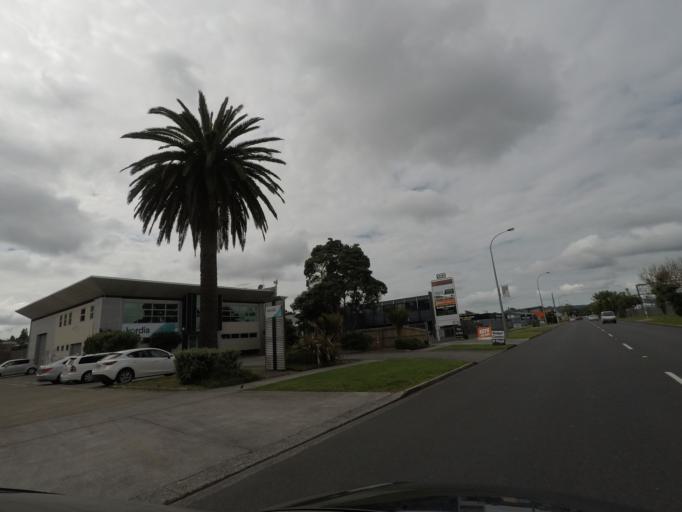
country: NZ
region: Auckland
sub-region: Auckland
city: Waitakere
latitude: -36.8880
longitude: 174.6316
